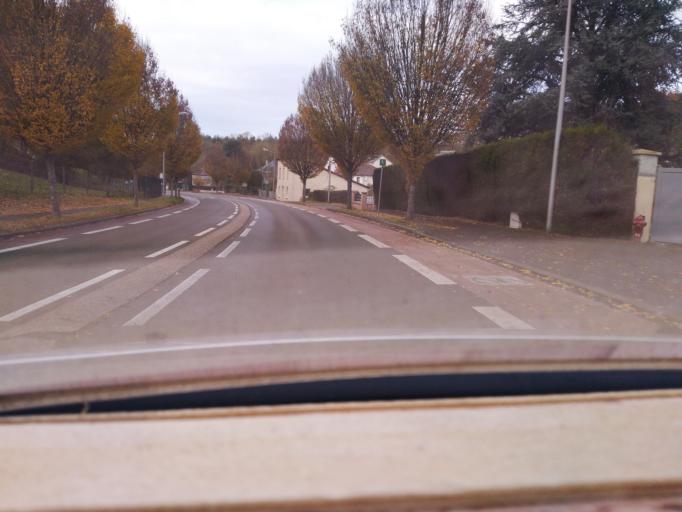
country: FR
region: Haute-Normandie
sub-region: Departement de la Seine-Maritime
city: Canteleu
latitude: 49.4443
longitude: 1.0167
